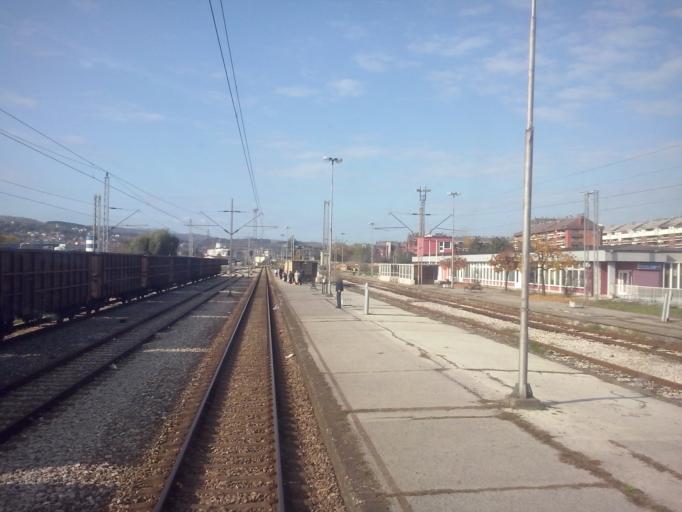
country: RS
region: Central Serbia
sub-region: Kolubarski Okrug
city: Valjevo
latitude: 44.2707
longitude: 19.9083
